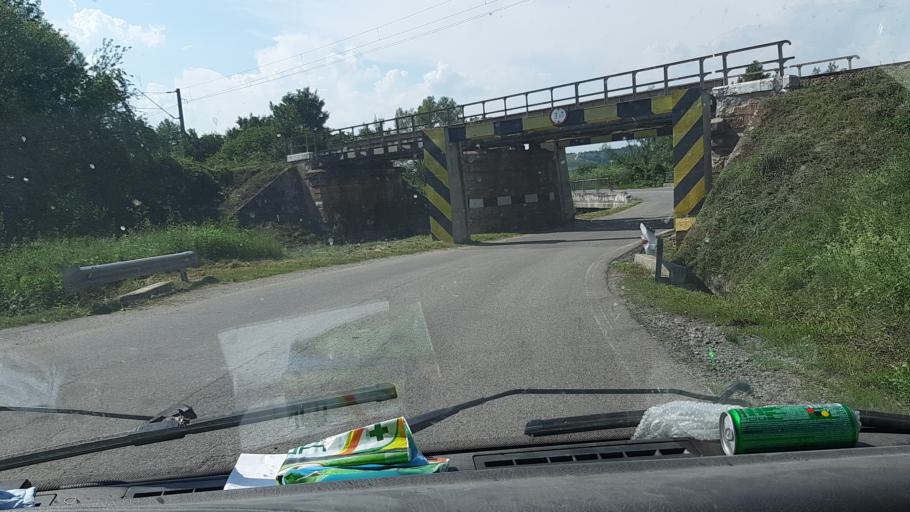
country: RO
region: Caras-Severin
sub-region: Comuna Ezeris
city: Ezeris
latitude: 45.3985
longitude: 21.9146
